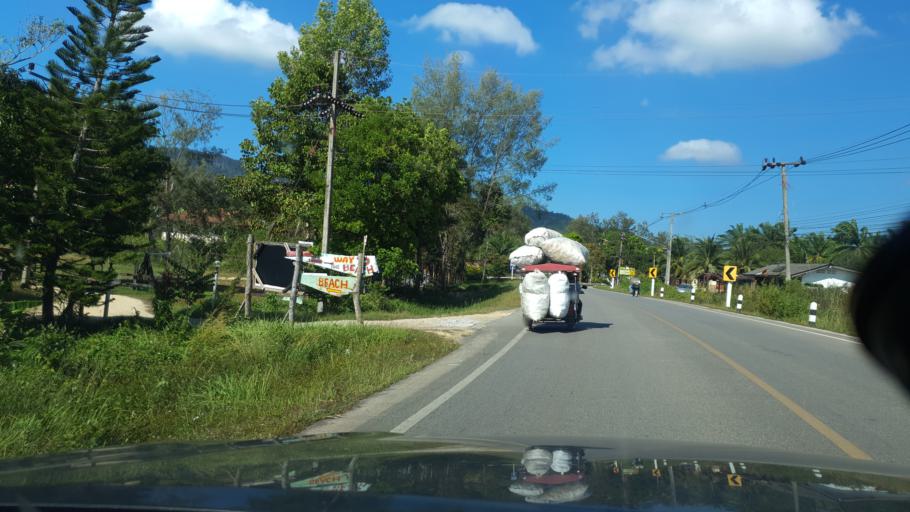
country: TH
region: Krabi
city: Krabi
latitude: 8.0290
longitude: 98.8693
